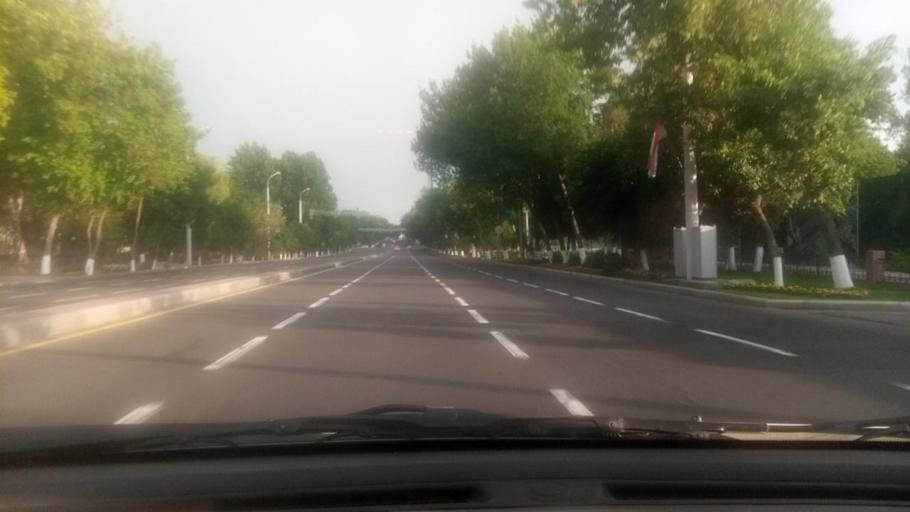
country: UZ
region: Toshkent
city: Salor
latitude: 41.3364
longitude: 69.3427
